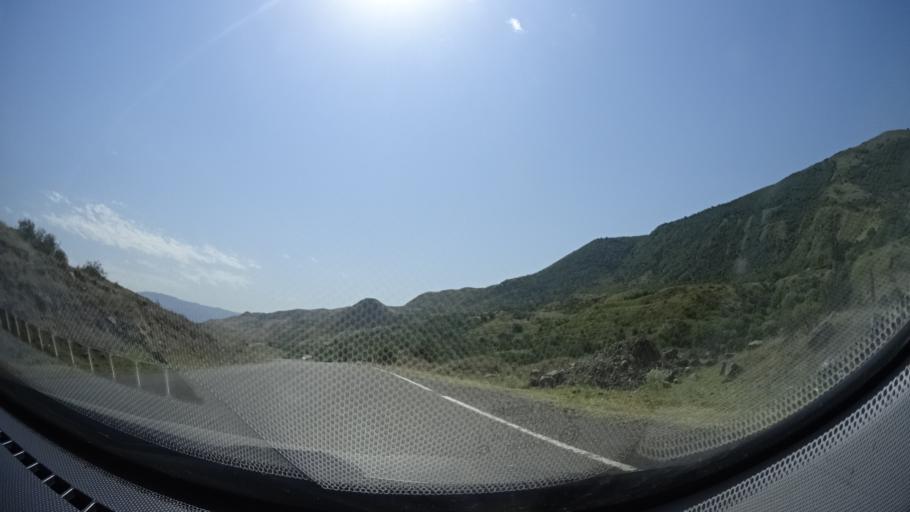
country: GE
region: Samtskhe-Javakheti
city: Aspindza
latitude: 41.5942
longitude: 43.1638
